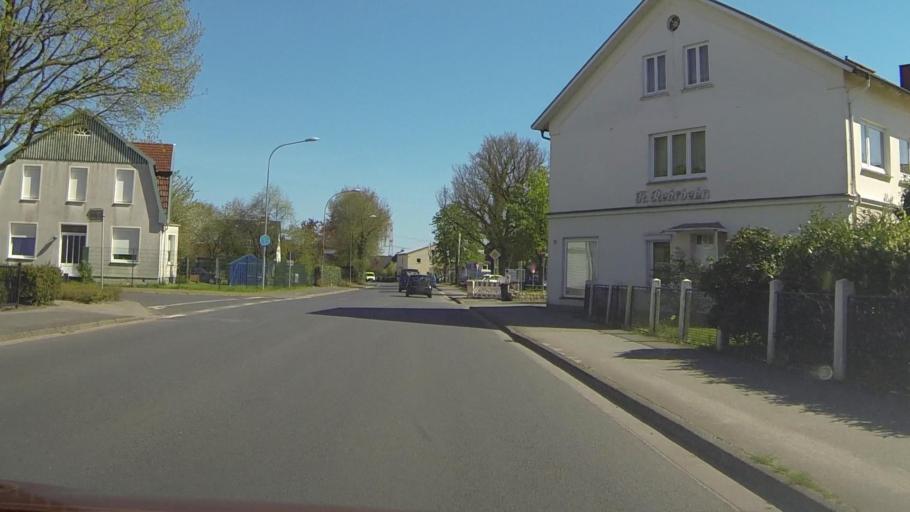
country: DE
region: Schleswig-Holstein
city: Tornesch
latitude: 53.6859
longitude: 9.7278
